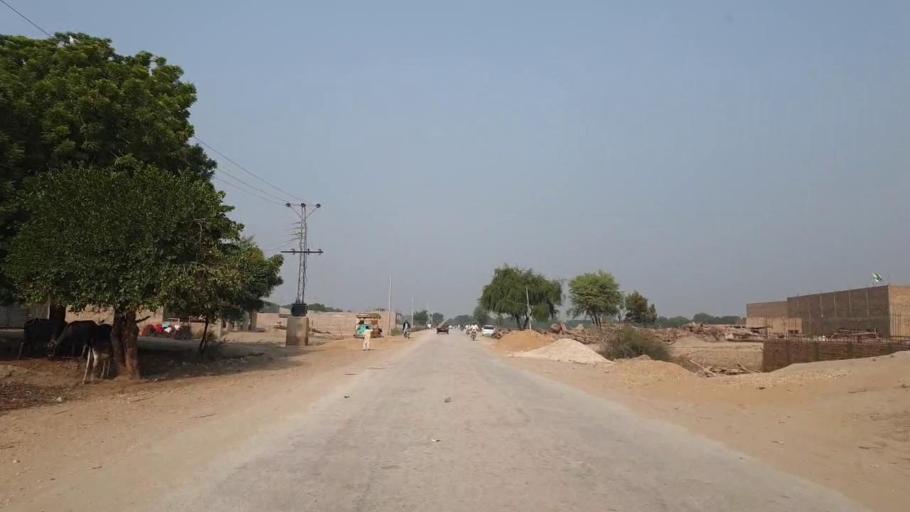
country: PK
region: Sindh
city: Bhan
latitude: 26.5684
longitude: 67.7253
